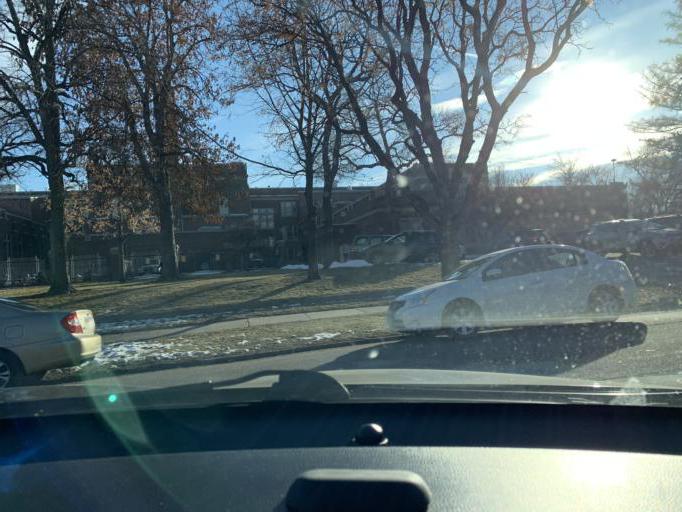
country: US
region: Colorado
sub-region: Adams County
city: Berkley
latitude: 39.7732
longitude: -105.0323
